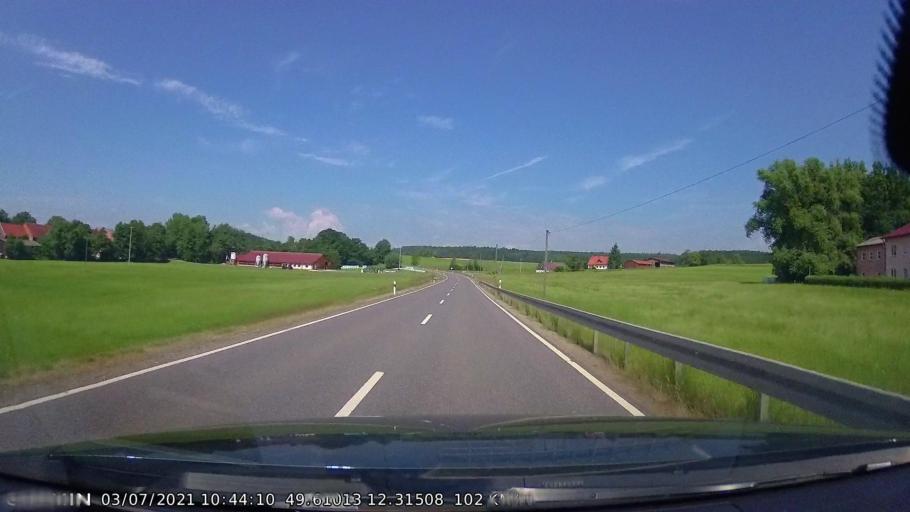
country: DE
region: Bavaria
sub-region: Upper Palatinate
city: Vohenstrauss
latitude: 49.6102
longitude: 12.3148
